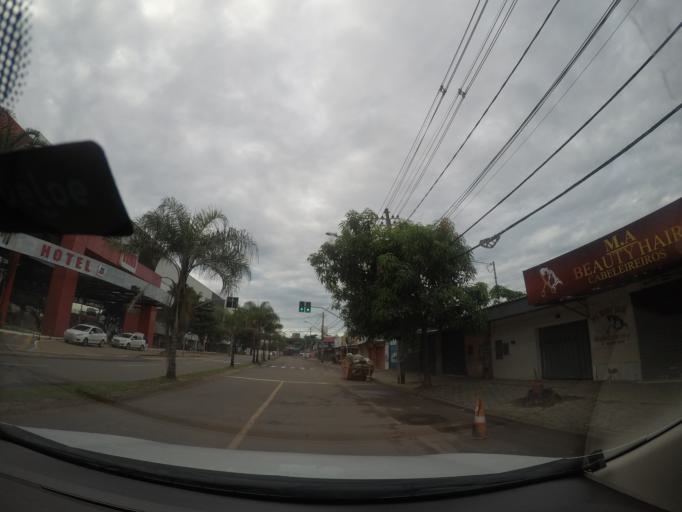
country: BR
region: Goias
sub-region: Goiania
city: Goiania
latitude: -16.6609
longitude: -49.2628
